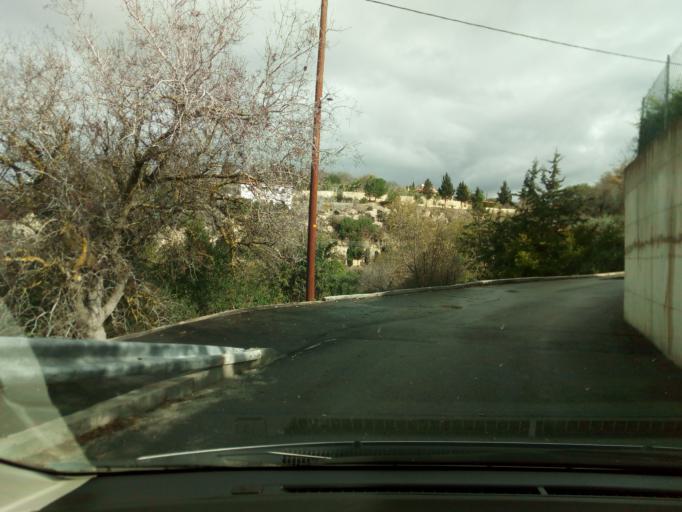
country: CY
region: Pafos
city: Tala
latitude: 34.9232
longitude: 32.5137
